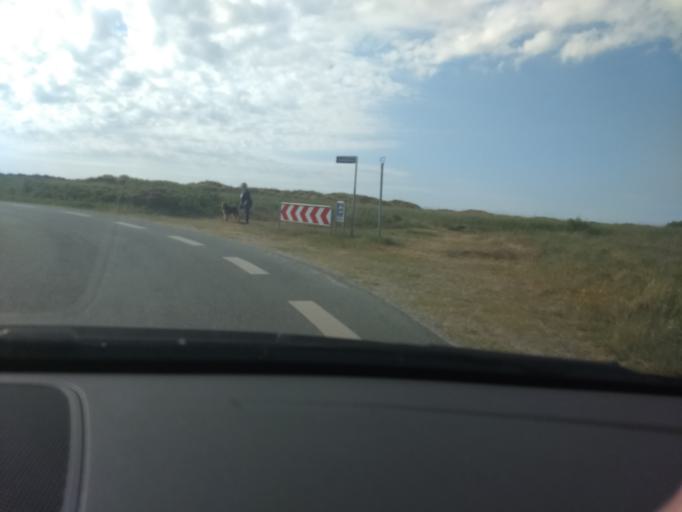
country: DE
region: Schleswig-Holstein
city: List
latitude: 55.1322
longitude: 8.4938
